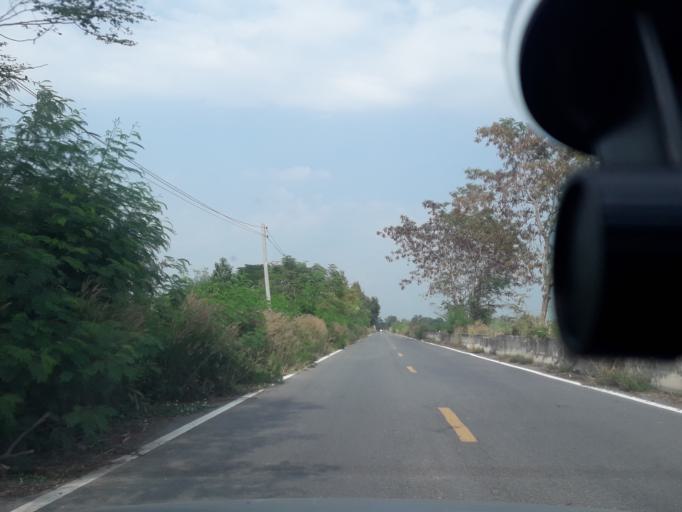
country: TH
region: Sara Buri
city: Nong Khae
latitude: 14.2704
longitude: 100.8913
